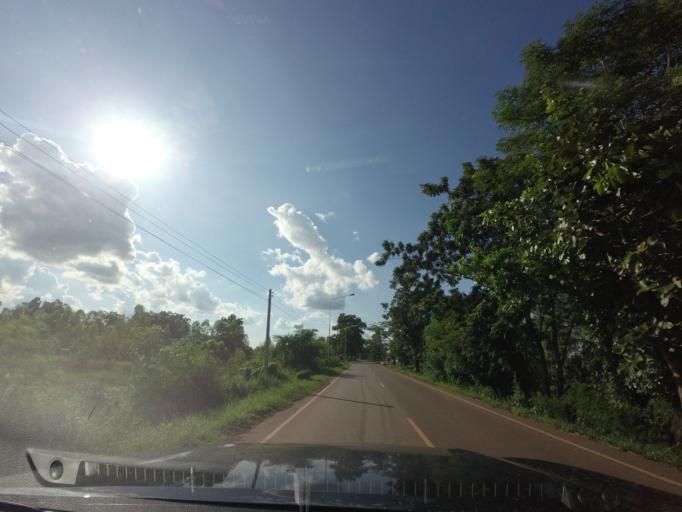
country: TH
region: Changwat Udon Thani
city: Ban Dung
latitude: 17.7404
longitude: 103.3441
